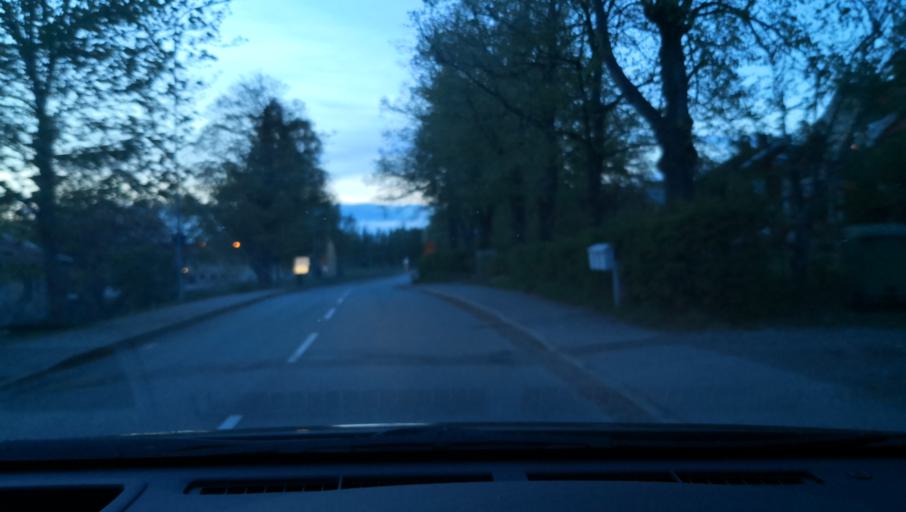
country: SE
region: OErebro
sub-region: Lekebergs Kommun
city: Fjugesta
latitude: 59.0262
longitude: 14.8667
